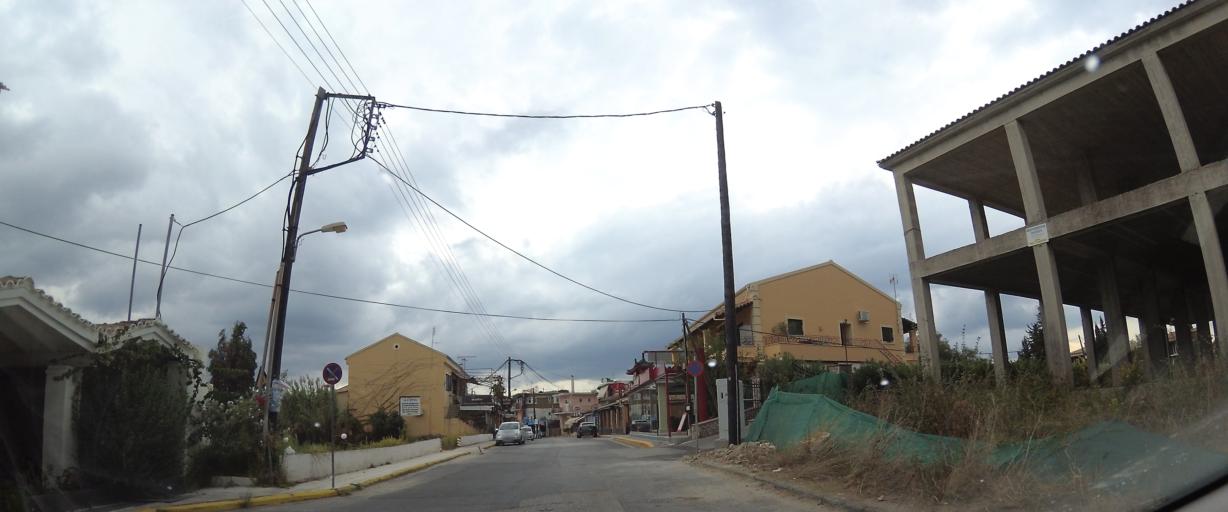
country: GR
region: Ionian Islands
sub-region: Nomos Kerkyras
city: Kontokali
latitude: 39.6512
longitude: 19.8453
